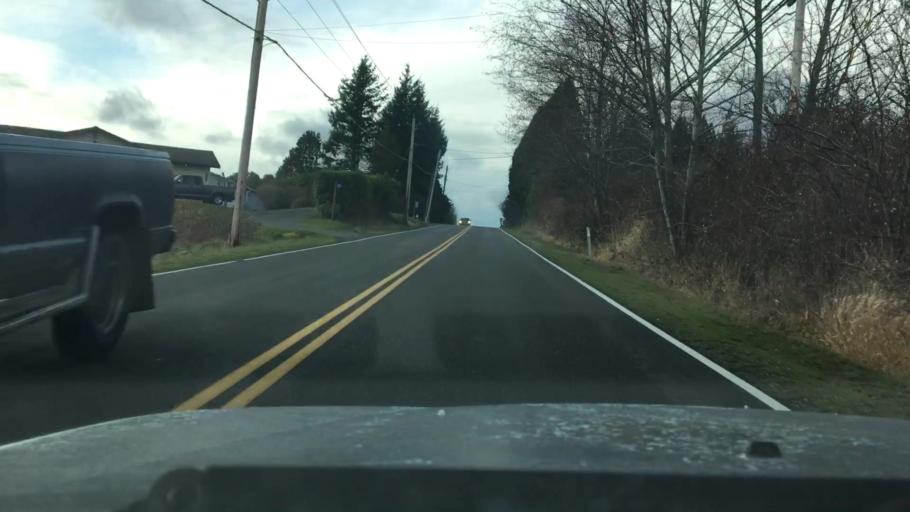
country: US
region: Washington
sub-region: Whatcom County
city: Ferndale
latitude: 48.8484
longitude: -122.6198
